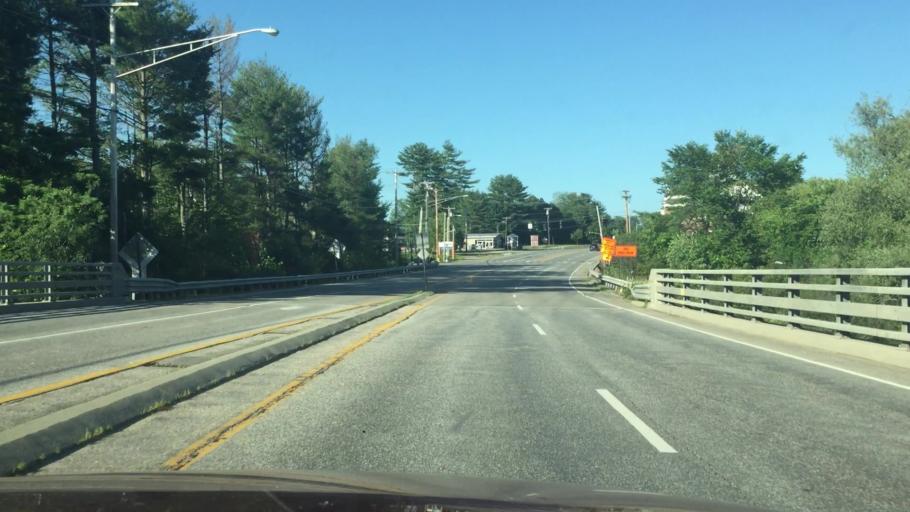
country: US
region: Maine
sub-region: Cumberland County
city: Yarmouth
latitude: 43.8026
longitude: -70.1843
